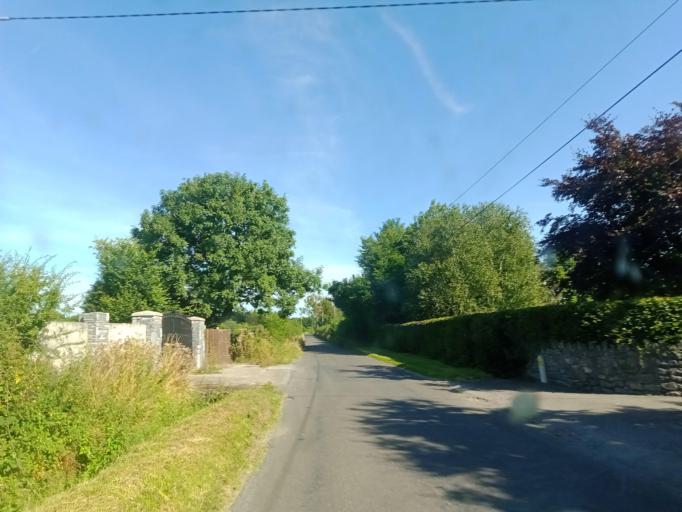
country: IE
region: Leinster
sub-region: Kilkenny
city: Ballyragget
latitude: 52.7440
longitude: -7.3985
